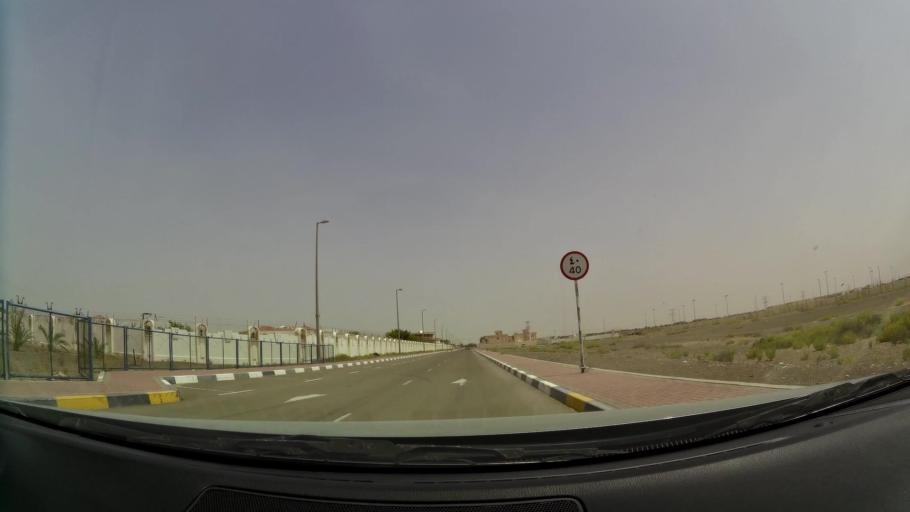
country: AE
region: Abu Dhabi
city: Al Ain
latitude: 24.1882
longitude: 55.6700
